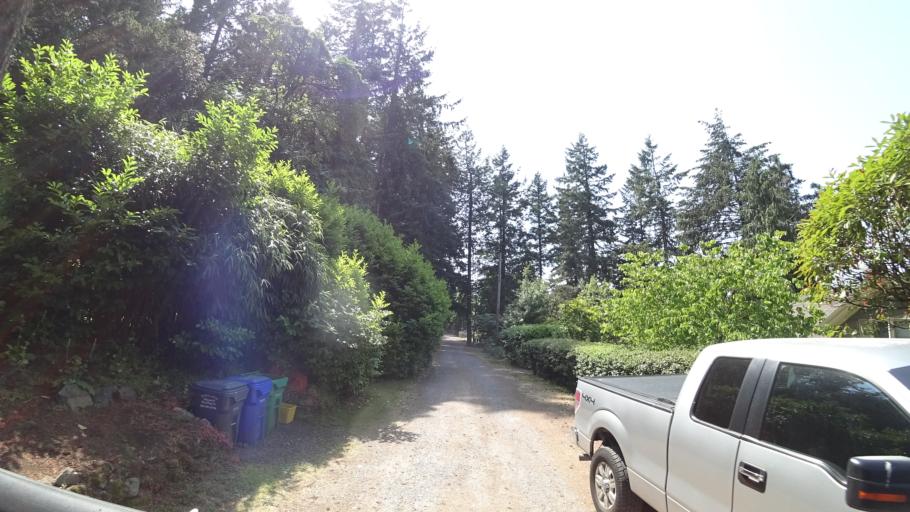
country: US
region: Oregon
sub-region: Multnomah County
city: Lents
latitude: 45.5166
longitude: -122.5954
